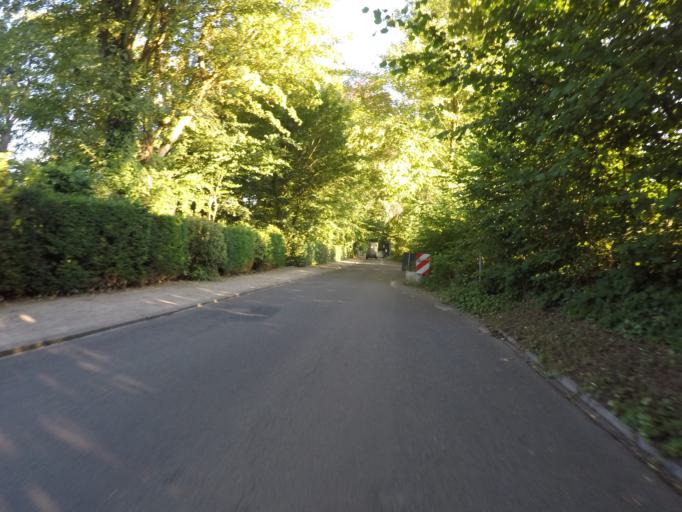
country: DE
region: Hamburg
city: Wohldorf-Ohlstedt
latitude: 53.6878
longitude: 10.1147
